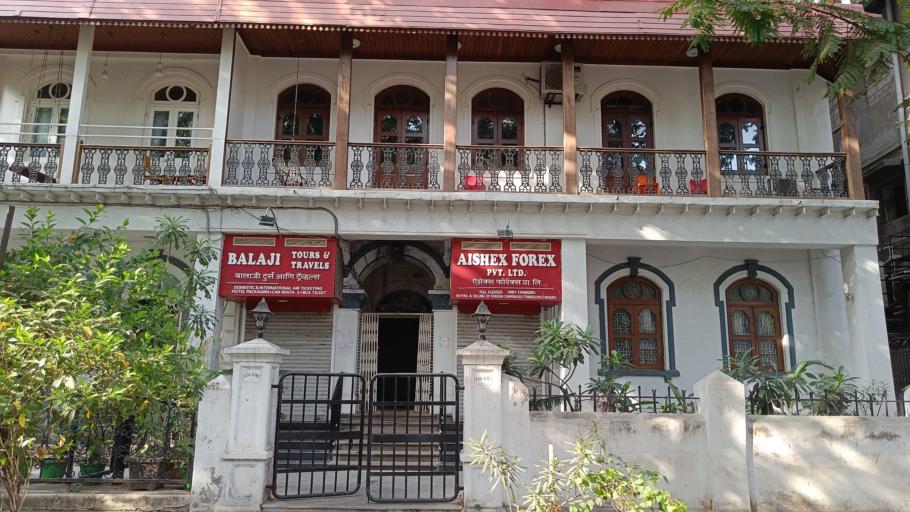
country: IN
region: Maharashtra
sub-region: Raigarh
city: Uran
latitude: 18.9217
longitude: 72.8316
